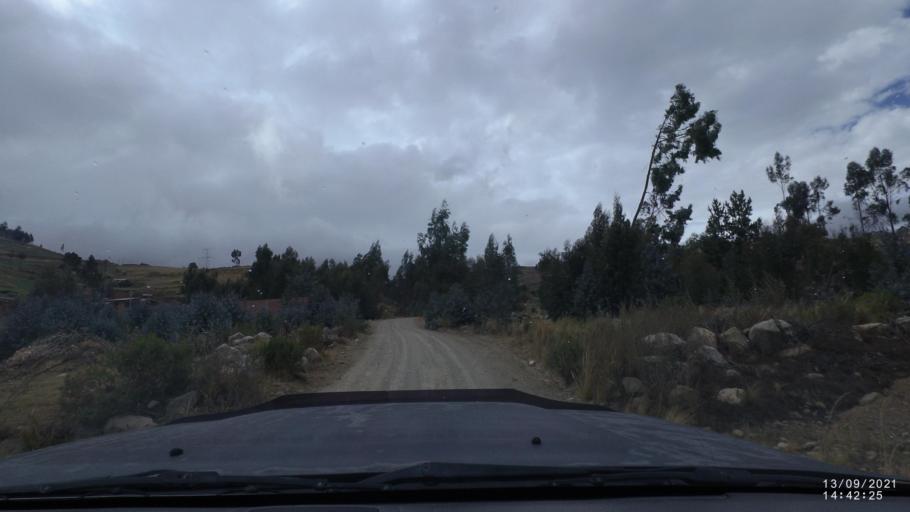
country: BO
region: Cochabamba
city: Colomi
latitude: -17.3638
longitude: -65.8144
